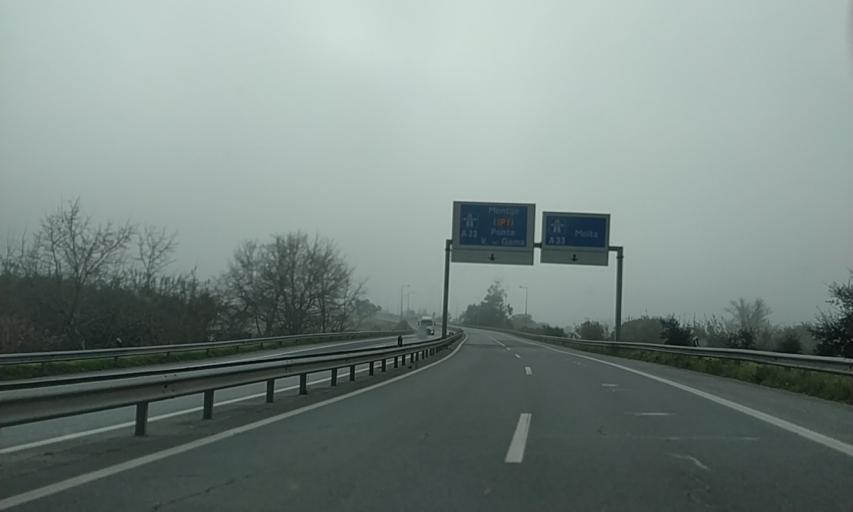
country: PT
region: Setubal
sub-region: Montijo
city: Montijo
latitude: 38.6820
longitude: -8.9481
